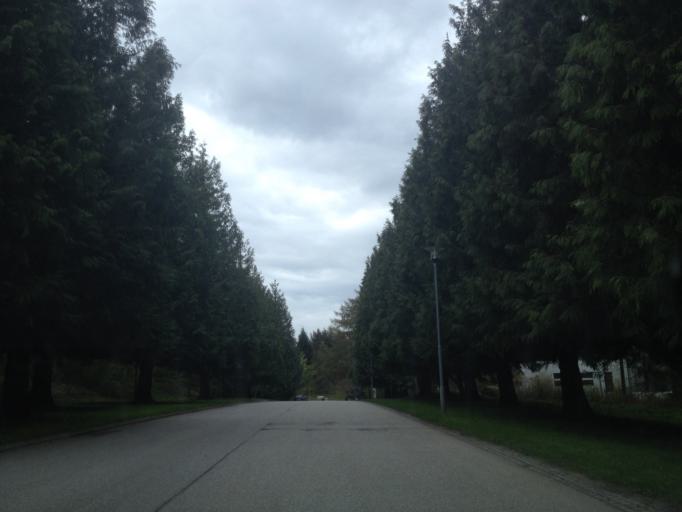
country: DK
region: Capital Region
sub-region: Horsholm Kommune
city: Horsholm
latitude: 55.8733
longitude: 12.4920
